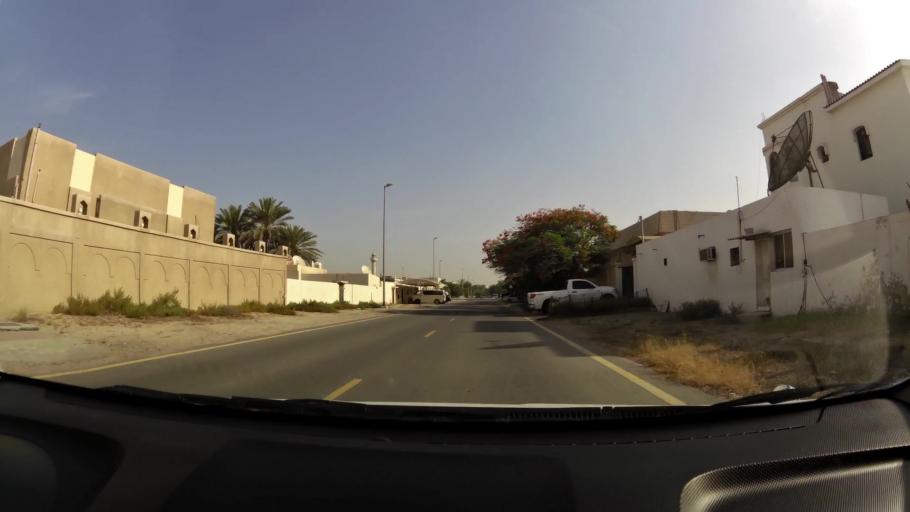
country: AE
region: Ash Shariqah
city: Sharjah
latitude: 25.2460
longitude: 55.4110
